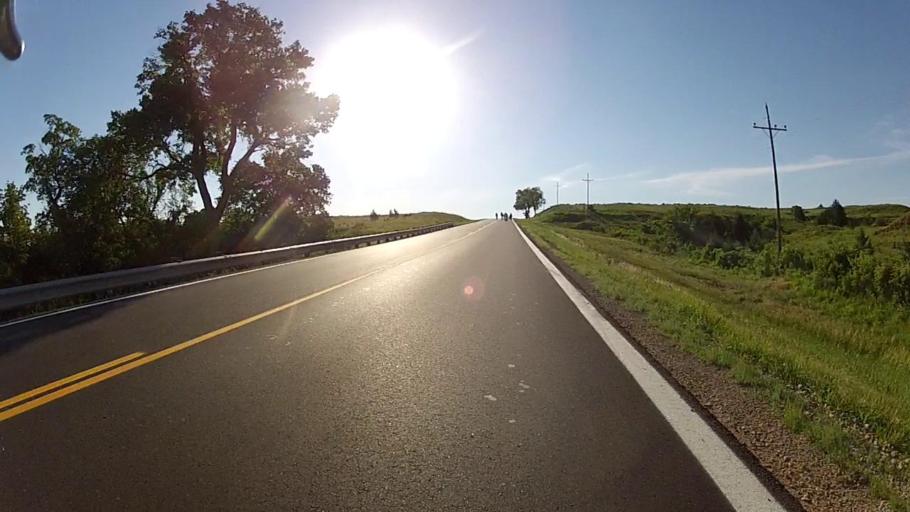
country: US
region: Kansas
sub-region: Comanche County
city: Coldwater
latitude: 37.2819
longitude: -99.0746
